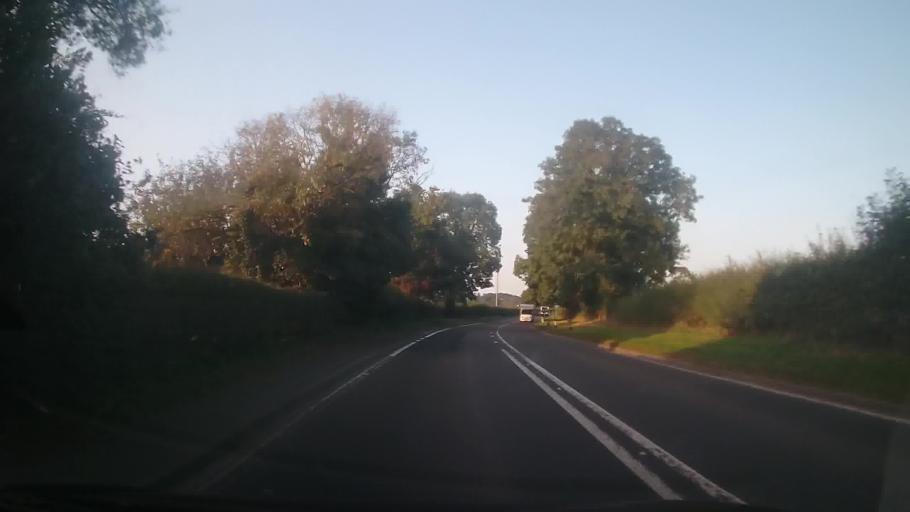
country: GB
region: Wales
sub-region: Sir Powys
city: Welshpool
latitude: 52.6268
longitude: -3.1666
